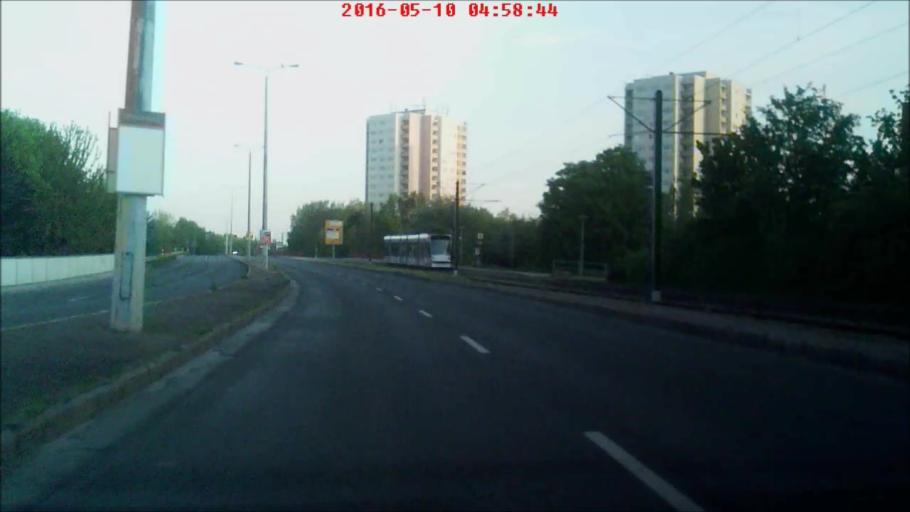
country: DE
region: Thuringia
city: Erfurt
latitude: 51.0048
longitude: 11.0014
